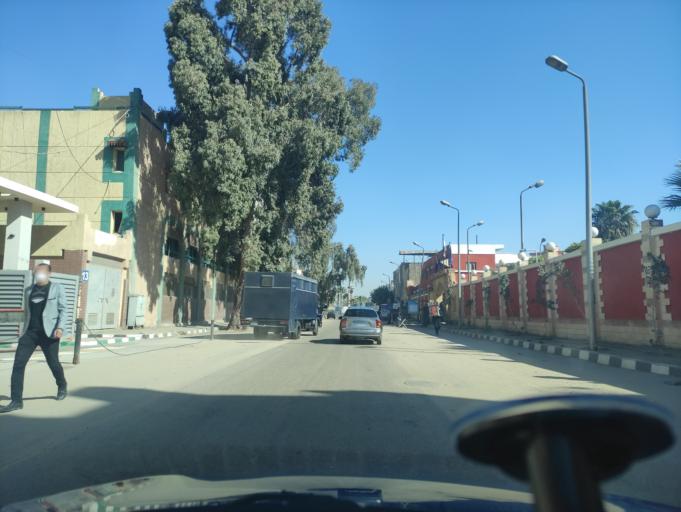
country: EG
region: Muhafazat al Qahirah
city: Cairo
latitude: 30.0542
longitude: 31.2760
